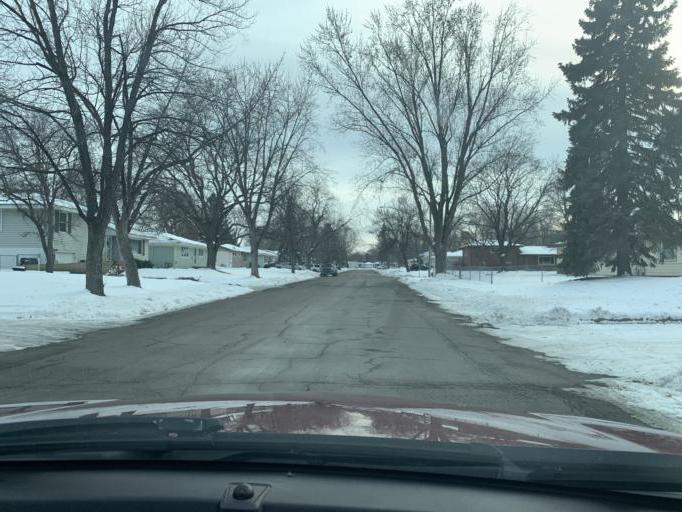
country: US
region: Minnesota
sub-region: Washington County
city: Saint Paul Park
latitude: 44.8363
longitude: -92.9754
